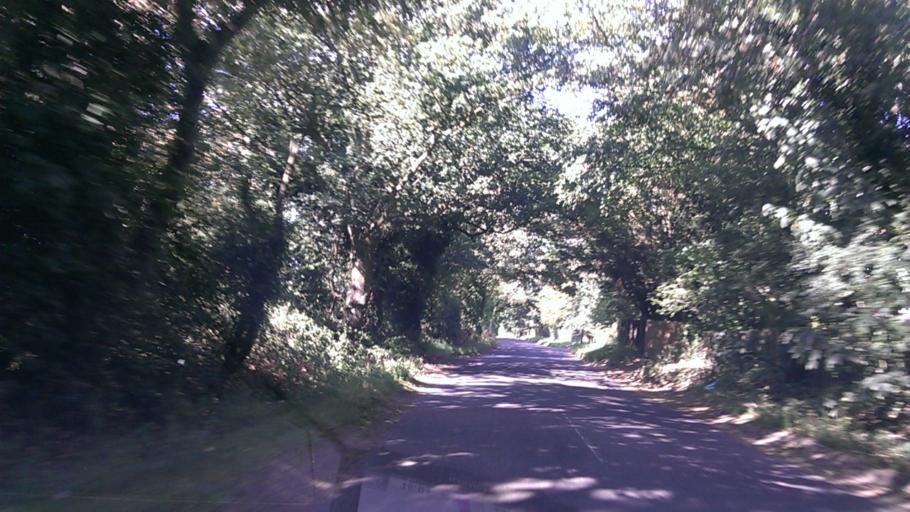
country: GB
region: England
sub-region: Essex
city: Layer de la Haye
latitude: 51.8577
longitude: 0.8829
